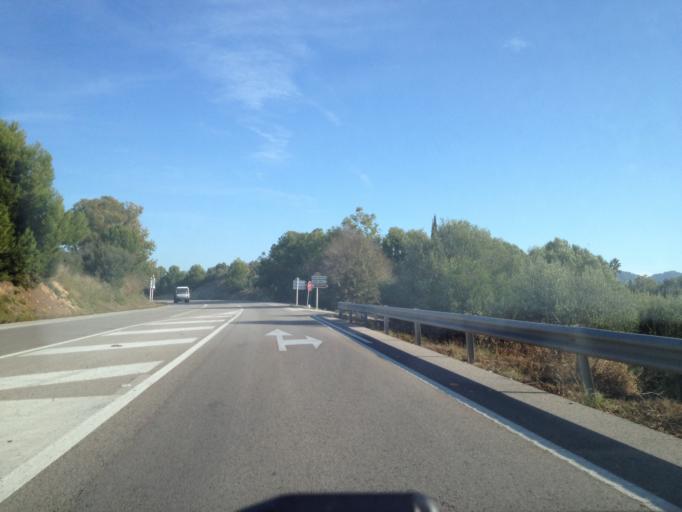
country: ES
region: Balearic Islands
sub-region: Illes Balears
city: Son Servera
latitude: 39.6439
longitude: 3.3754
